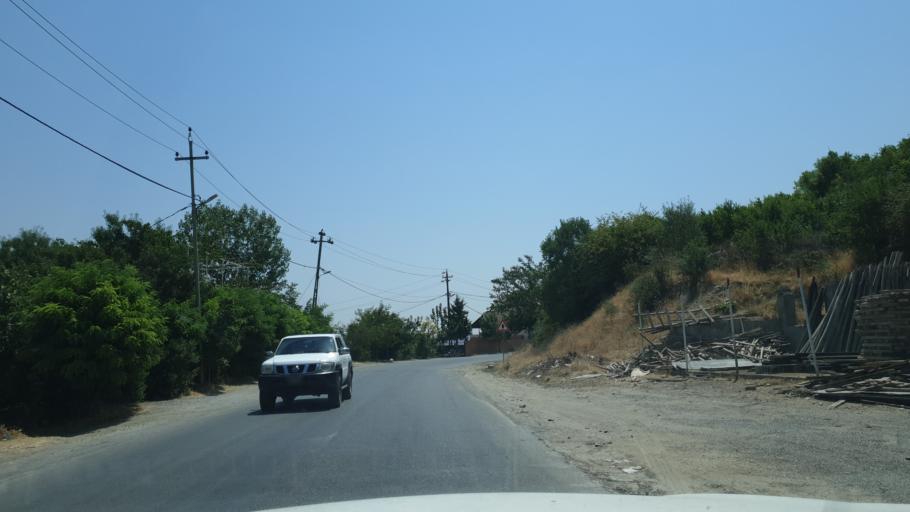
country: IQ
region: Arbil
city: Nahiyat Hiran
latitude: 36.2830
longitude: 44.4915
